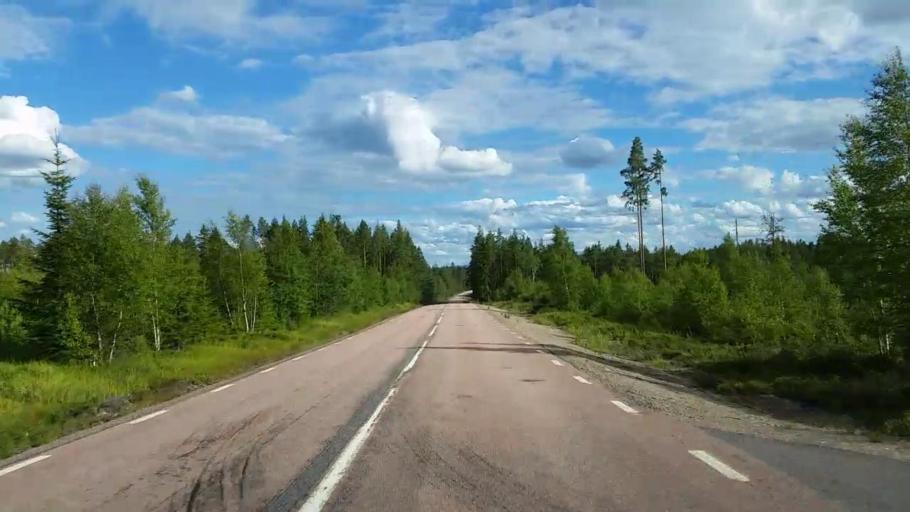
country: SE
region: Gaevleborg
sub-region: Ljusdals Kommun
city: Farila
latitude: 61.9583
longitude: 15.8792
